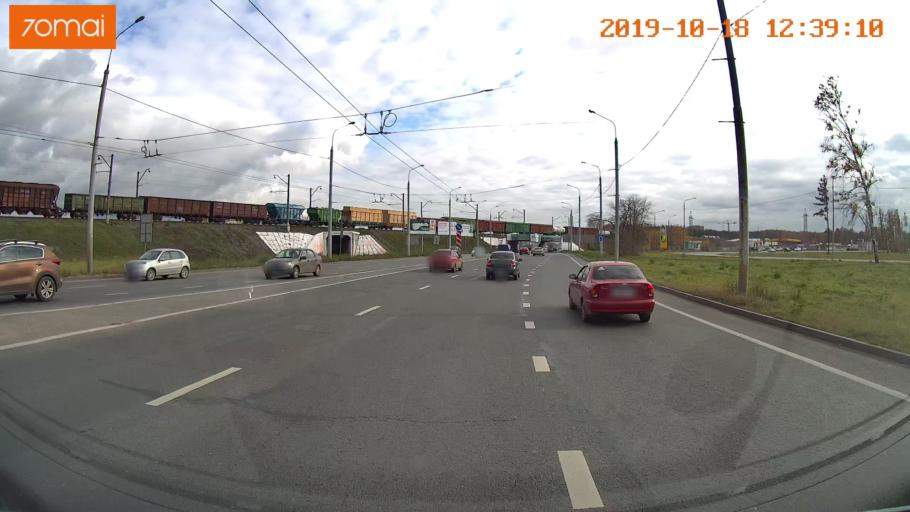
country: RU
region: Rjazan
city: Ryazan'
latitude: 54.6516
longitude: 39.6403
